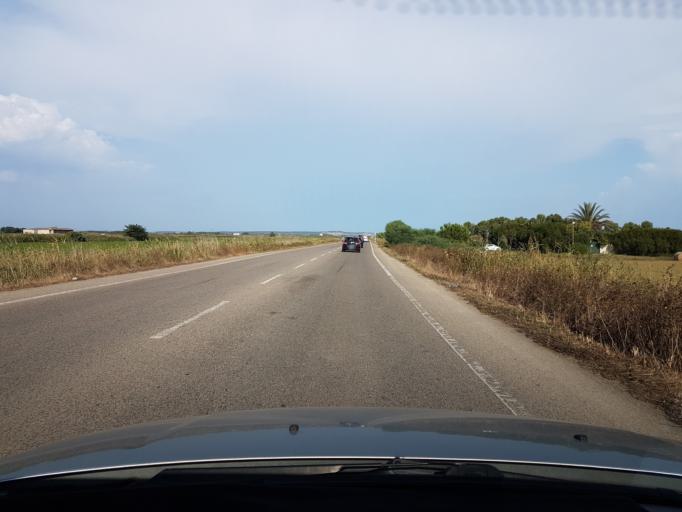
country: IT
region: Sardinia
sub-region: Provincia di Oristano
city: Cabras
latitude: 39.9180
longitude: 8.5279
